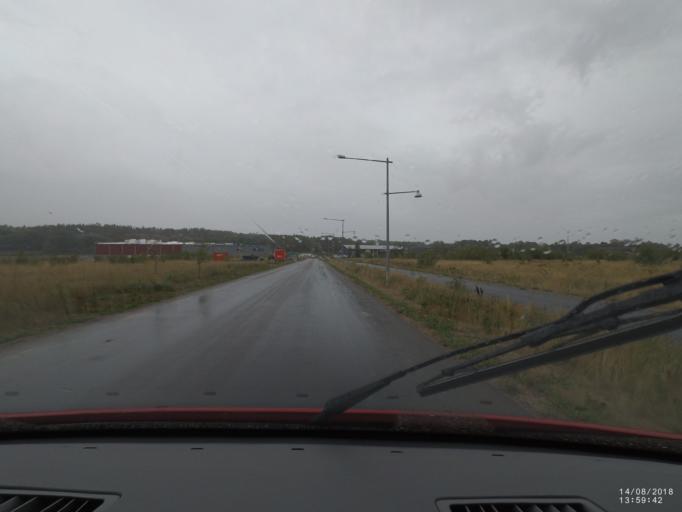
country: SE
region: Soedermanland
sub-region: Nykopings Kommun
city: Nykoping
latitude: 58.7536
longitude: 16.9703
